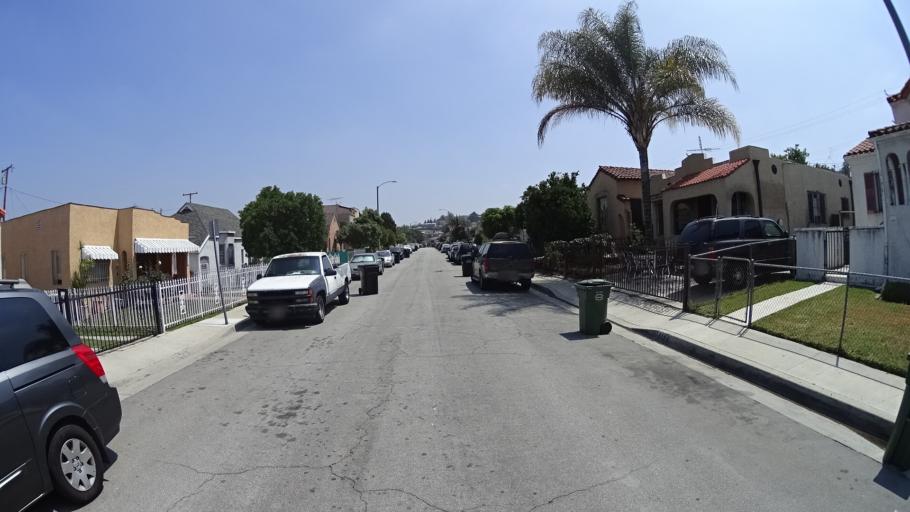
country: US
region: California
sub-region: Los Angeles County
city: Belvedere
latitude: 34.0572
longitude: -118.1760
